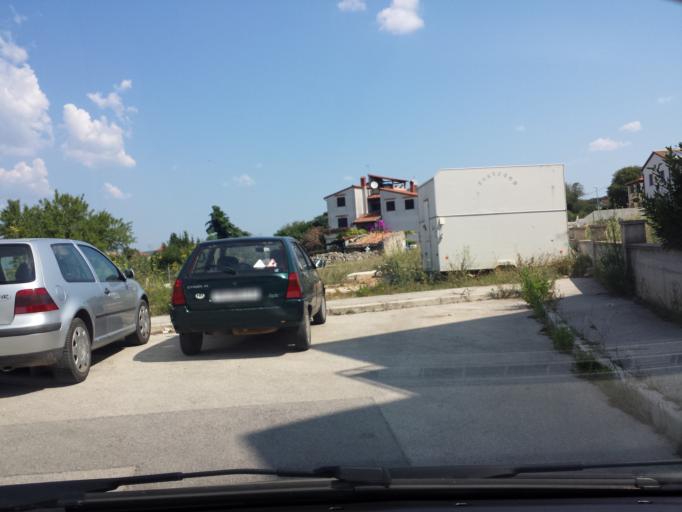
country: HR
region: Istarska
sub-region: Grad Pula
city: Pula
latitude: 44.8971
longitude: 13.8491
